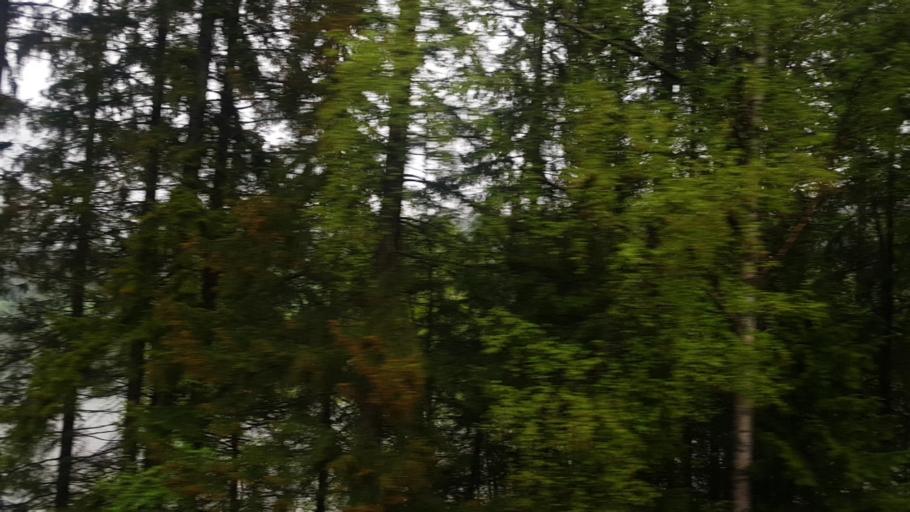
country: NO
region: Oppland
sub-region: Oyer
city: Tretten
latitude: 61.3110
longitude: 10.2907
